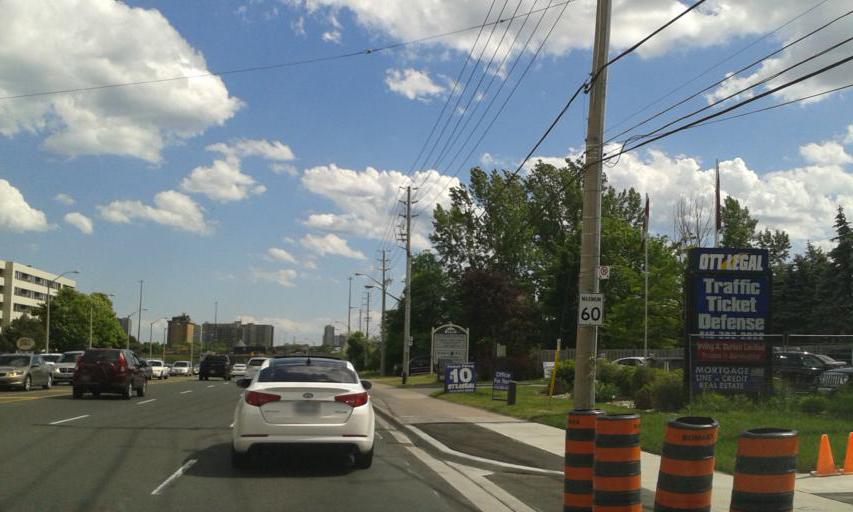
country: CA
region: Ontario
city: Scarborough
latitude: 43.7895
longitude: -79.2371
